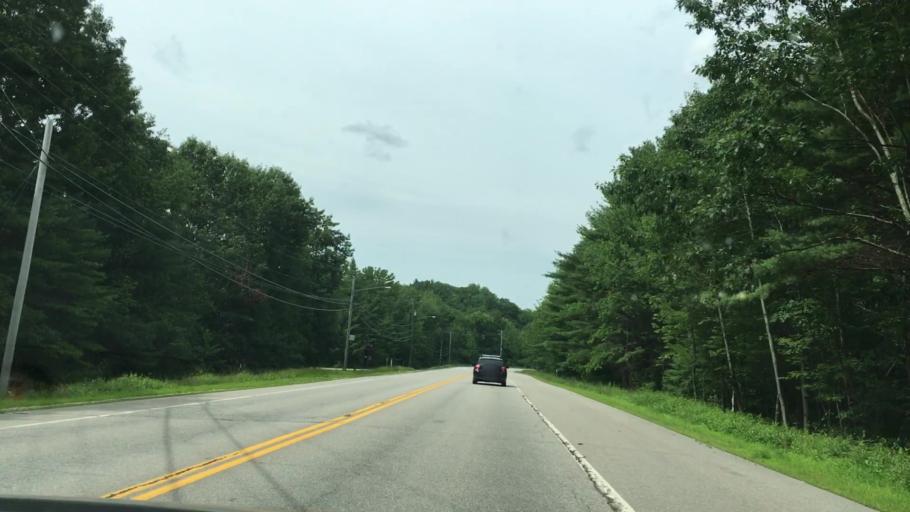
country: US
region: New Hampshire
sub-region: Hillsborough County
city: Peterborough
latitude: 42.8491
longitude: -71.9651
